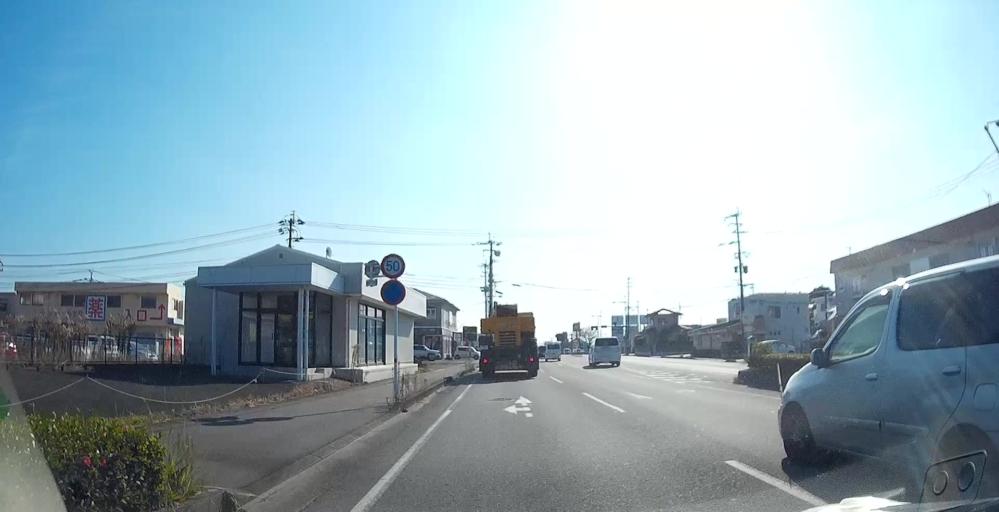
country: JP
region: Kumamoto
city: Kumamoto
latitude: 32.7846
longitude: 130.6734
